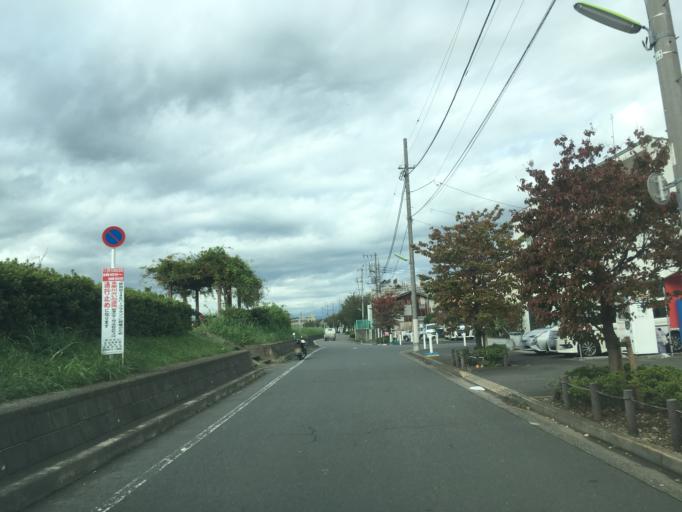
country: JP
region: Tokyo
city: Chofugaoka
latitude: 35.6191
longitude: 139.6022
